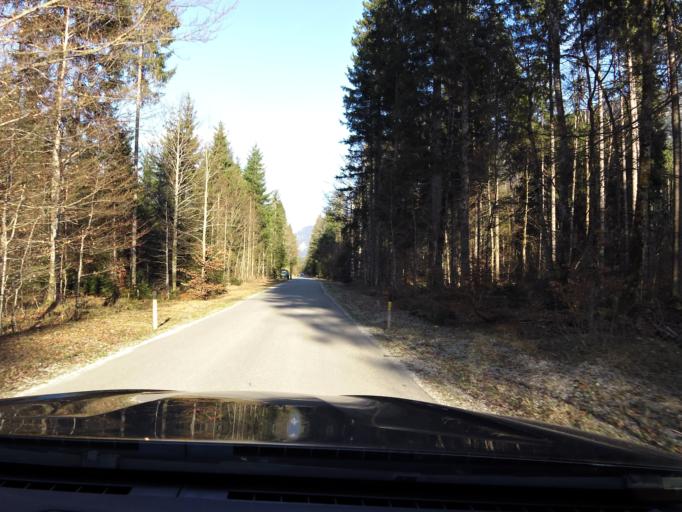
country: DE
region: Bavaria
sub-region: Upper Bavaria
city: Jachenau
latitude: 47.5479
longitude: 11.3747
